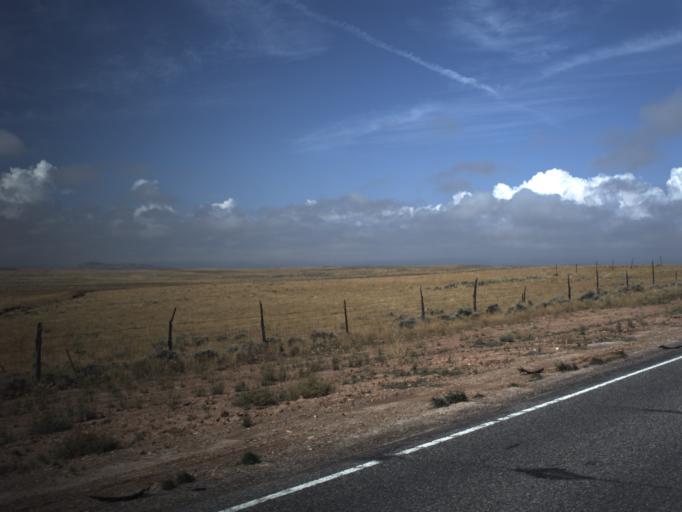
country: US
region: Wyoming
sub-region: Uinta County
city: Evanston
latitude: 41.4287
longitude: -111.0579
